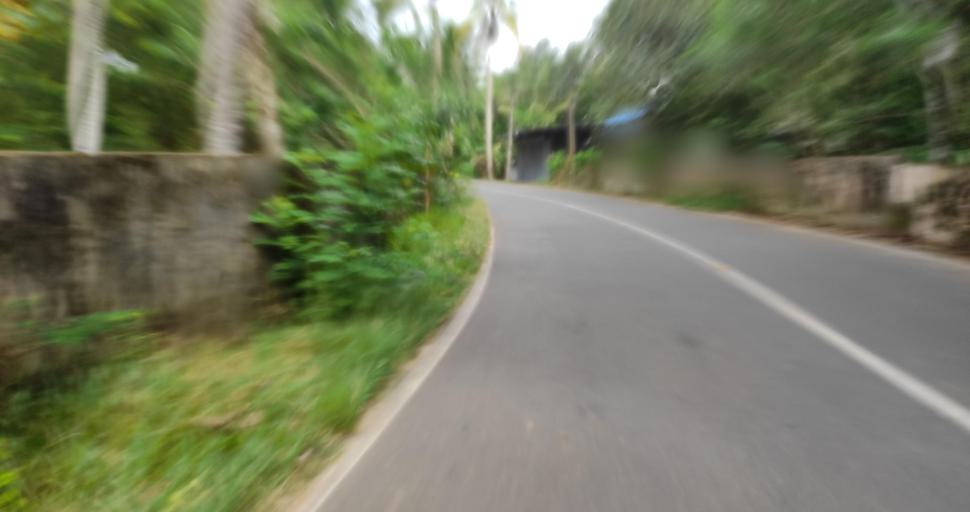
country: IN
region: Kerala
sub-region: Alappuzha
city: Vayalar
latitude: 9.6546
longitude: 76.3110
